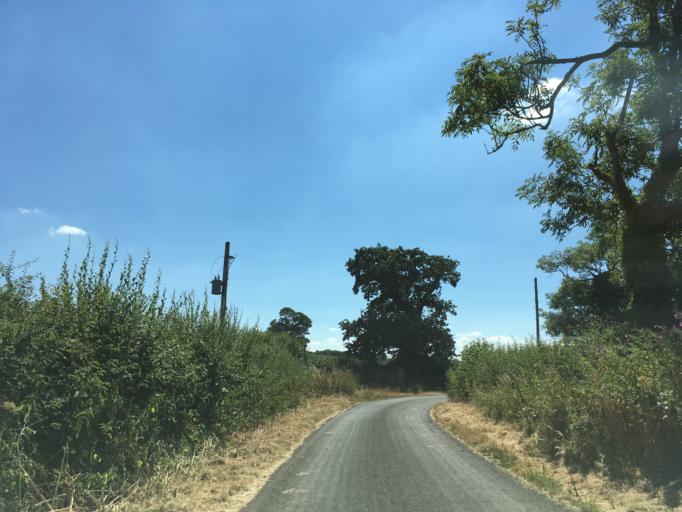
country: GB
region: England
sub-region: Wiltshire
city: Luckington
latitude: 51.5513
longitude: -2.2255
